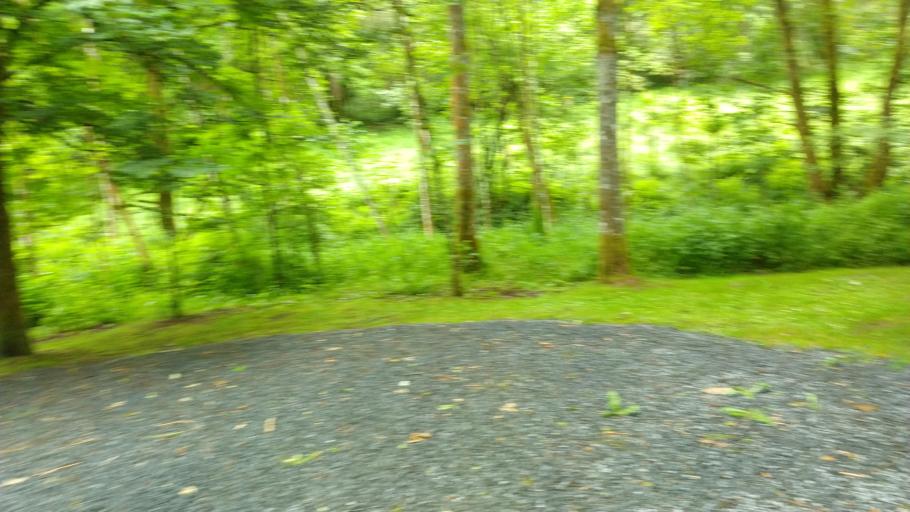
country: BE
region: Wallonia
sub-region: Province de Namur
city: Bievre
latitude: 49.9150
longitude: 4.9689
